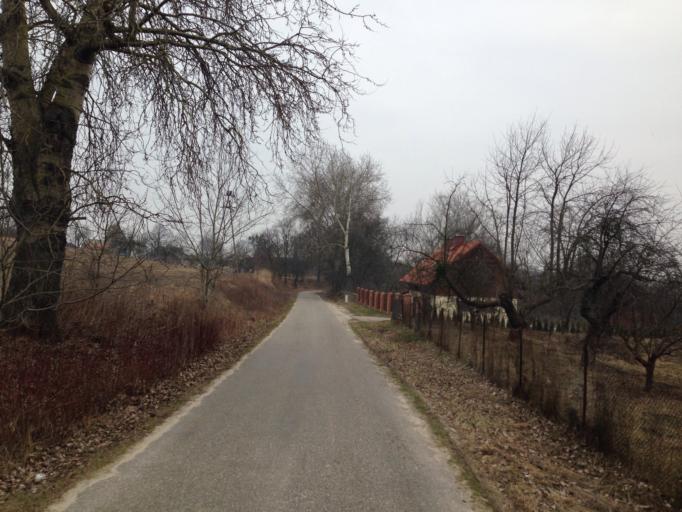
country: PL
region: Pomeranian Voivodeship
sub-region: Powiat kwidzynski
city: Sadlinki
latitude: 53.7309
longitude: 18.8229
